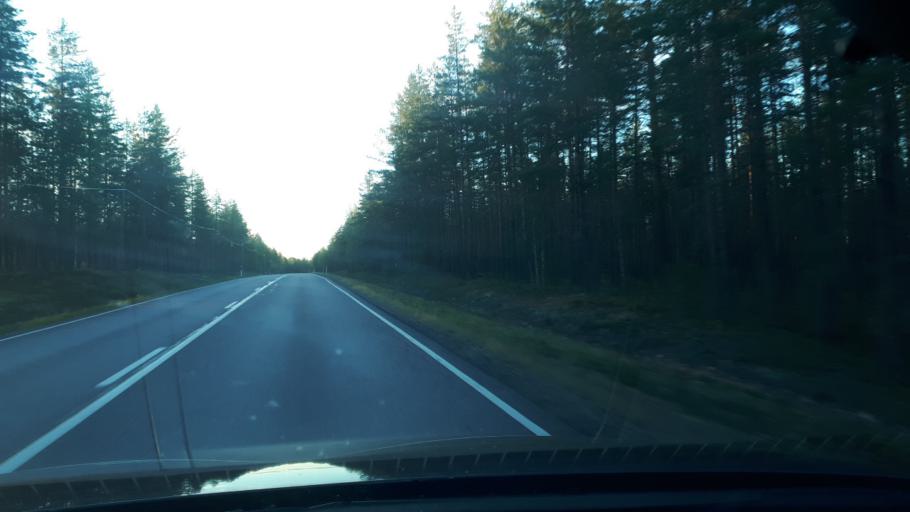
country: FI
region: Northern Ostrobothnia
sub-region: Haapavesi-Siikalatva
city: Pulkkila
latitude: 64.2221
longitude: 25.9122
